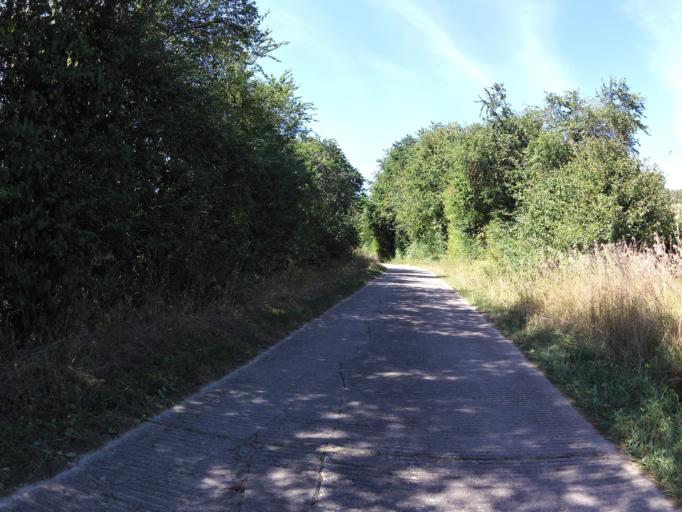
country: DE
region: Bavaria
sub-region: Regierungsbezirk Unterfranken
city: Guntersleben
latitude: 49.8660
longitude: 9.8962
